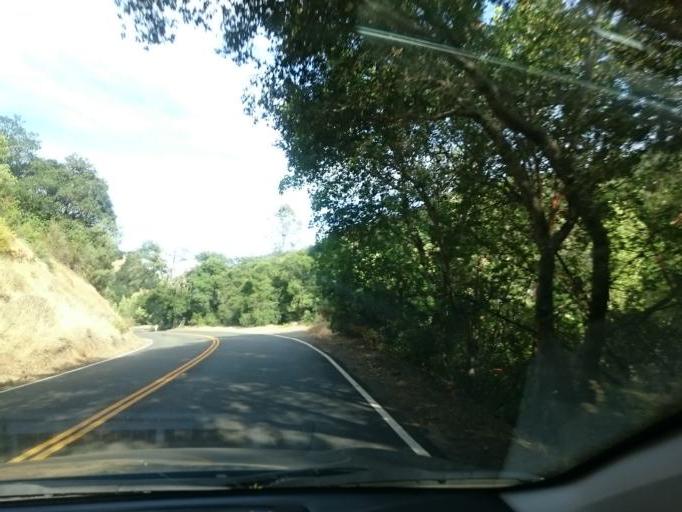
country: US
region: California
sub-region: Napa County
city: Yountville
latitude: 38.4901
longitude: -122.3252
